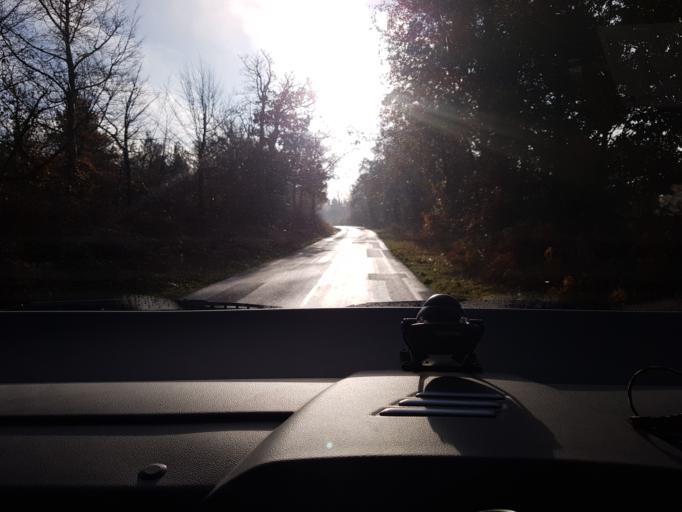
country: FR
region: Brittany
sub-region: Departement d'Ille-et-Vilaine
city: Fouillard
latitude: 48.1676
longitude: -1.5947
